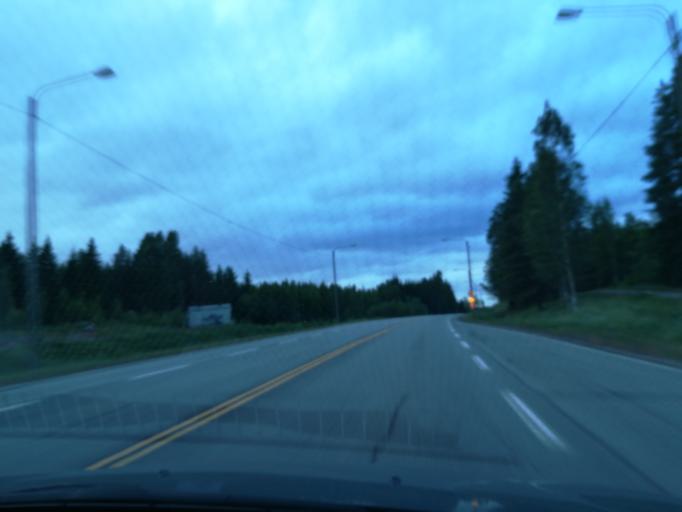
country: FI
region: Southern Savonia
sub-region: Mikkeli
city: Ristiina
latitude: 61.5005
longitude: 27.2384
